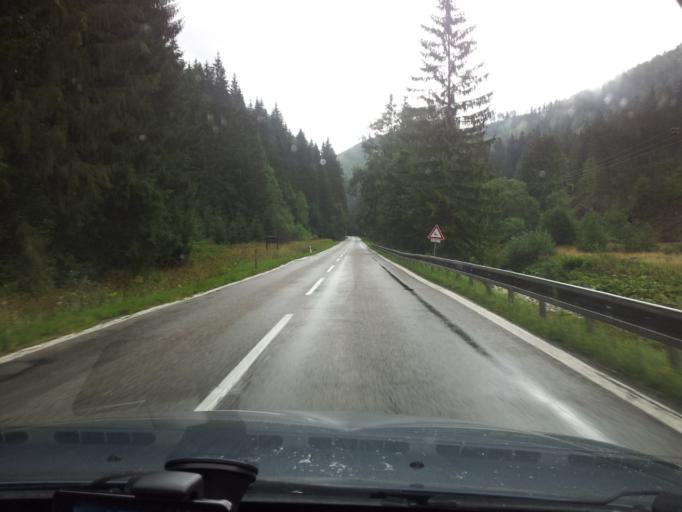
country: SK
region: Banskobystricky
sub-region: Okres Banska Bystrica
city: Brezno
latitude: 48.8674
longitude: 19.6483
